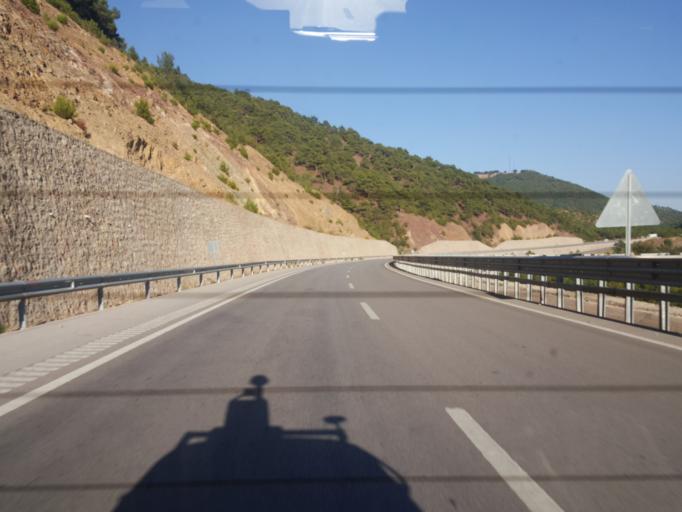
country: TR
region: Amasya
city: Akdag
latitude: 40.7540
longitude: 36.0658
